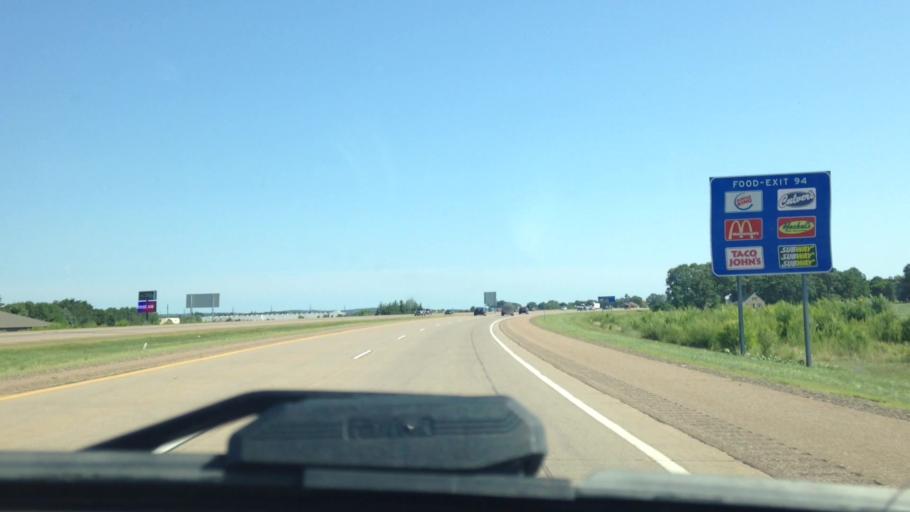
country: US
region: Wisconsin
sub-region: Chippewa County
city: Lake Hallie
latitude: 44.8732
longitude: -91.4206
